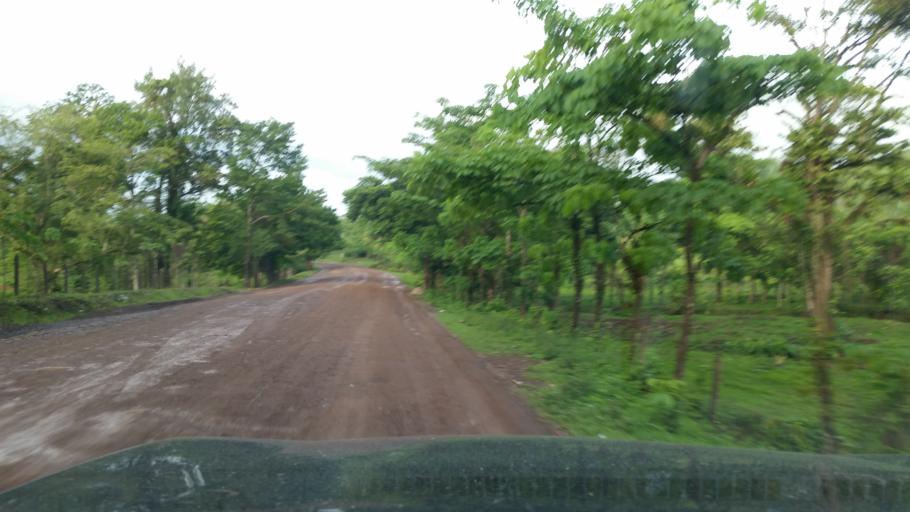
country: NI
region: Atlantico Norte (RAAN)
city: Siuna
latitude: 13.3664
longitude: -84.8766
